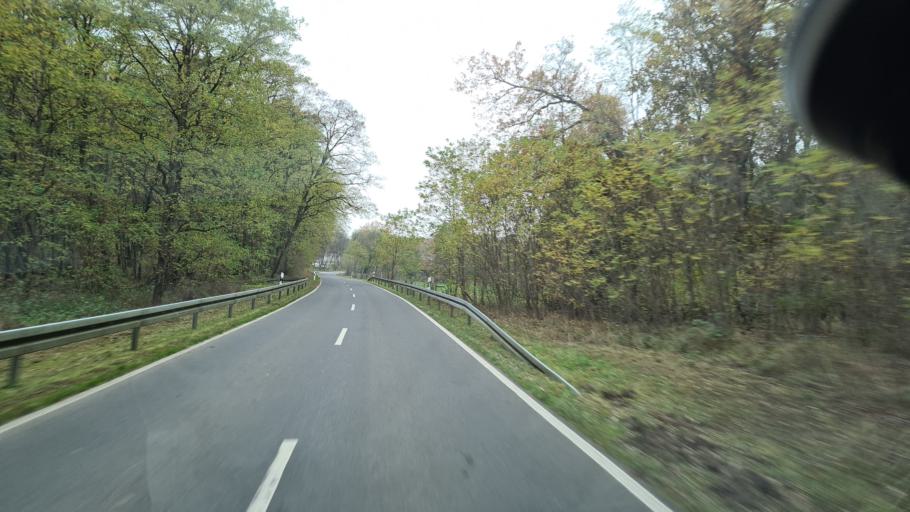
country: DE
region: Brandenburg
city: Lindow
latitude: 52.9612
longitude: 12.9974
